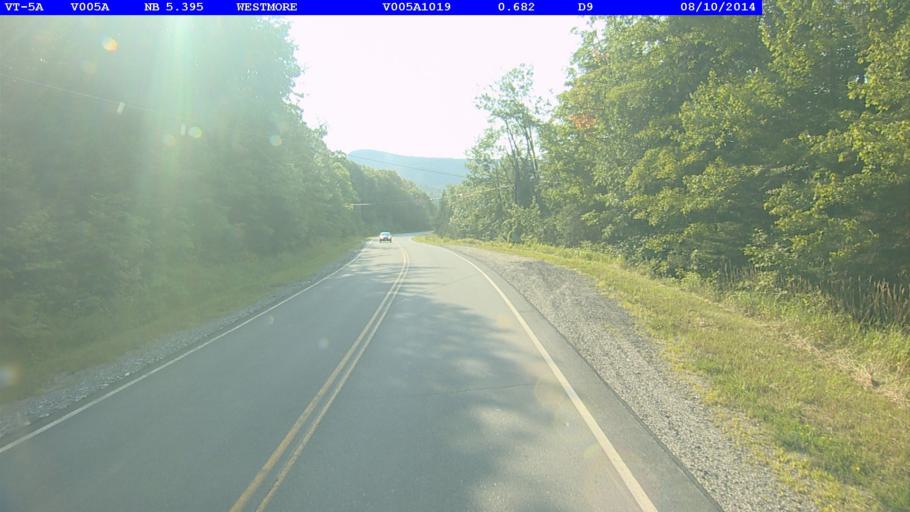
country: US
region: Vermont
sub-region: Caledonia County
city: Lyndonville
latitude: 44.7094
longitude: -72.0178
